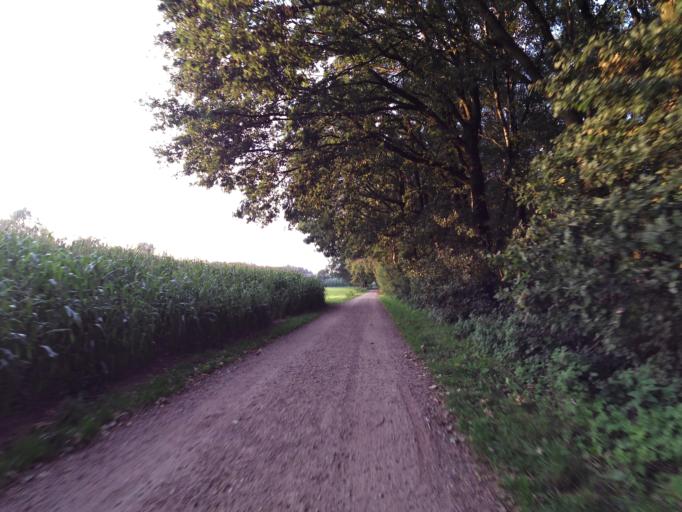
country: NL
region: Gelderland
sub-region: Gemeente Doesburg
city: Doesburg
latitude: 51.9549
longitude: 6.1977
